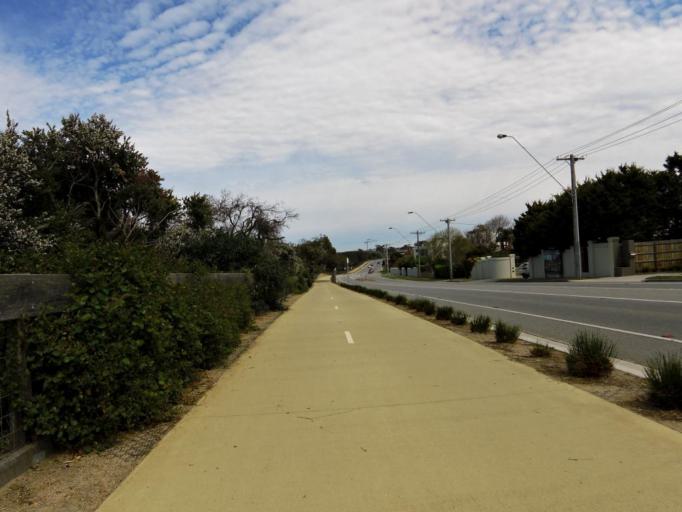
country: AU
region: Victoria
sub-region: Kingston
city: Mentone
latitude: -37.9868
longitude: 145.0506
